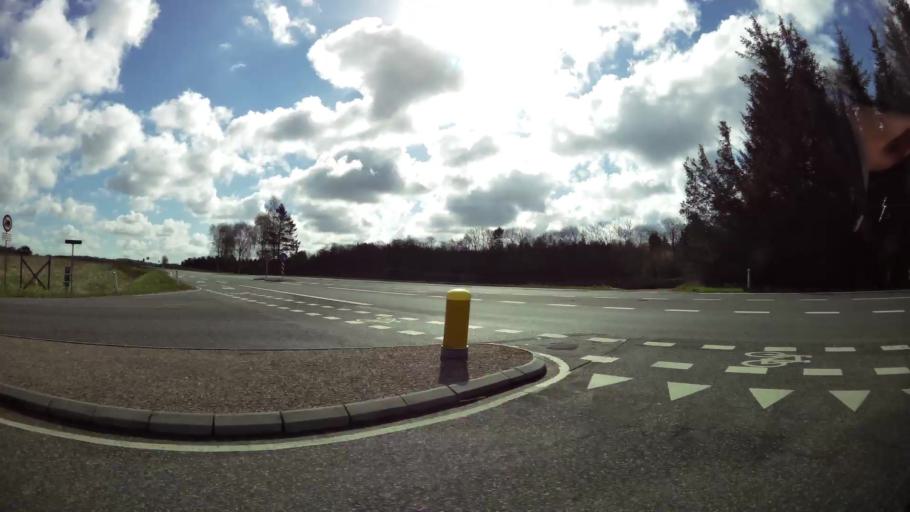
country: DK
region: North Denmark
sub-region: Mariagerfjord Kommune
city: Mariager
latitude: 56.6357
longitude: 9.9551
